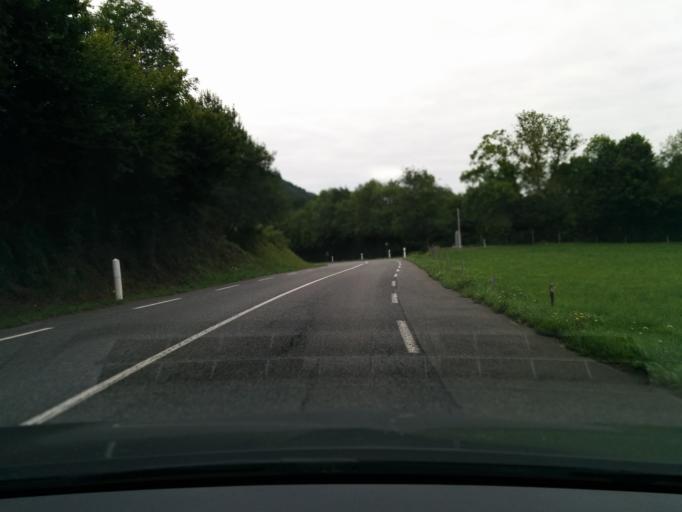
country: FR
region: Midi-Pyrenees
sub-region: Departement des Hautes-Pyrenees
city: La Barthe-de-Neste
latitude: 43.0094
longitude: 0.3746
